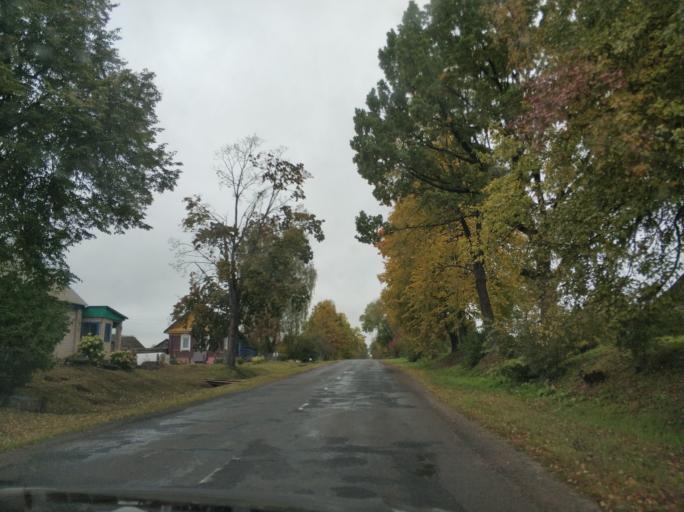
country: BY
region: Vitebsk
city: Polatsk
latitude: 55.4298
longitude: 28.9997
